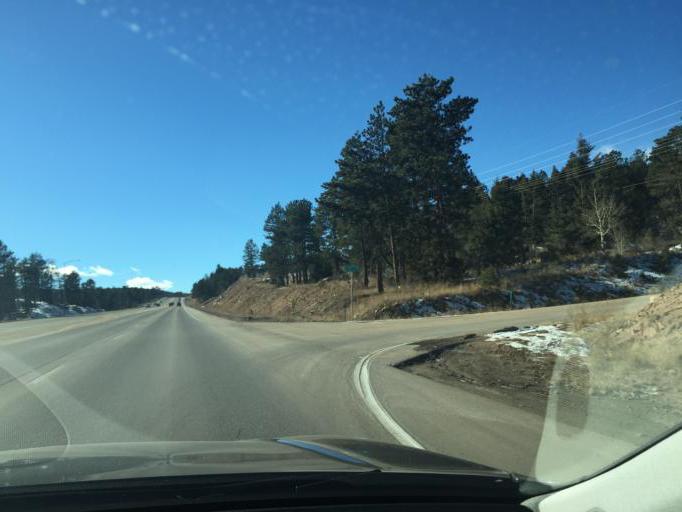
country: US
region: Colorado
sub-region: Jefferson County
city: Evergreen
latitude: 39.5065
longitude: -105.3128
